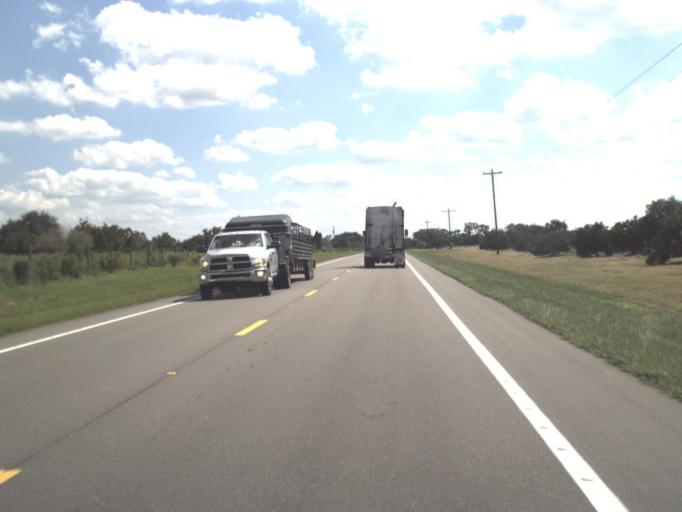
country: US
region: Florida
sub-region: Hardee County
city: Zolfo Springs
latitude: 27.4694
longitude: -81.7085
